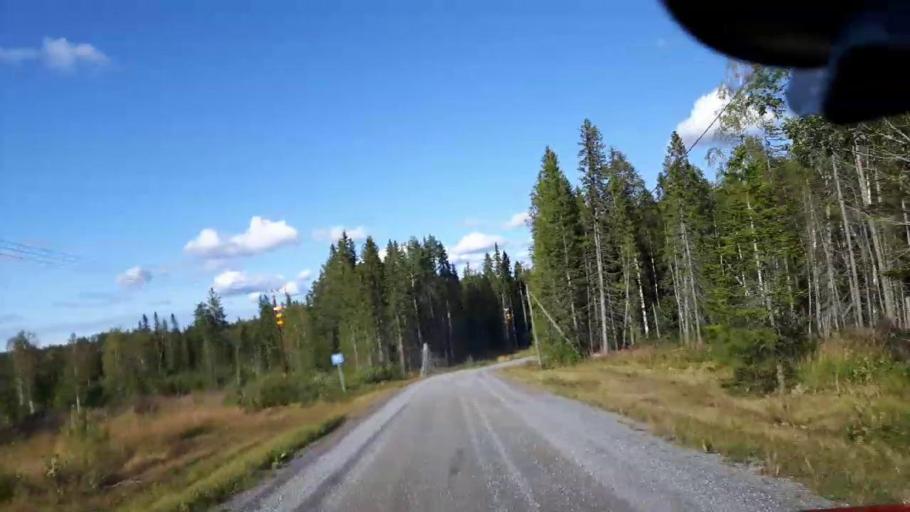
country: SE
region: Jaemtland
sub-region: Ragunda Kommun
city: Hammarstrand
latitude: 63.5128
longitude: 16.0496
